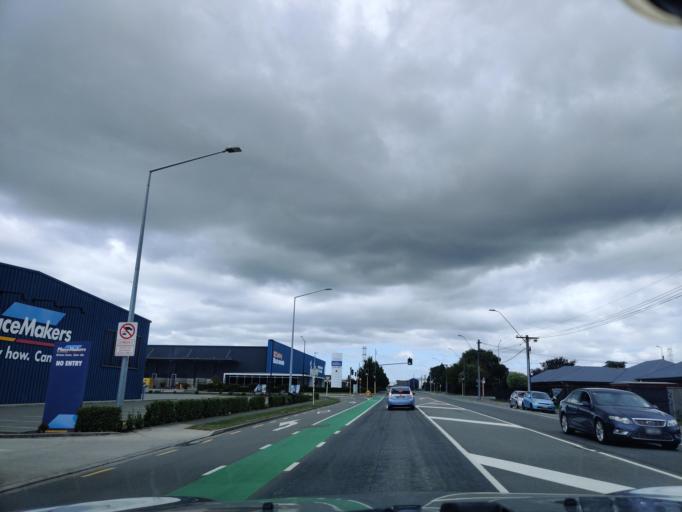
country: NZ
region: Canterbury
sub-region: Selwyn District
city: Prebbleton
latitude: -43.5474
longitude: 172.5213
